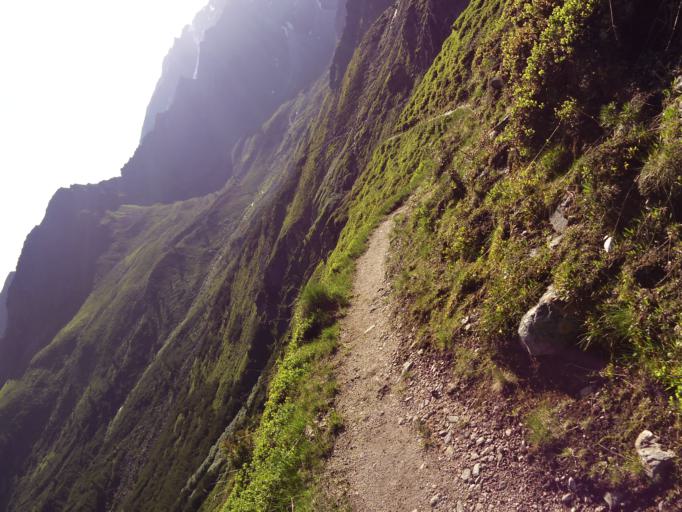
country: AT
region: Tyrol
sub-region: Politischer Bezirk Innsbruck Land
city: Gries im Sellrain
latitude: 47.0830
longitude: 11.1850
